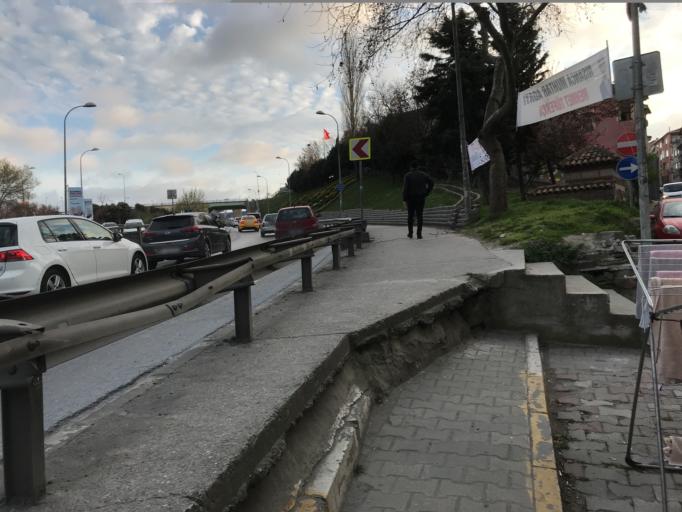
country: TR
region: Istanbul
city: Istanbul
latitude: 41.0409
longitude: 28.9366
